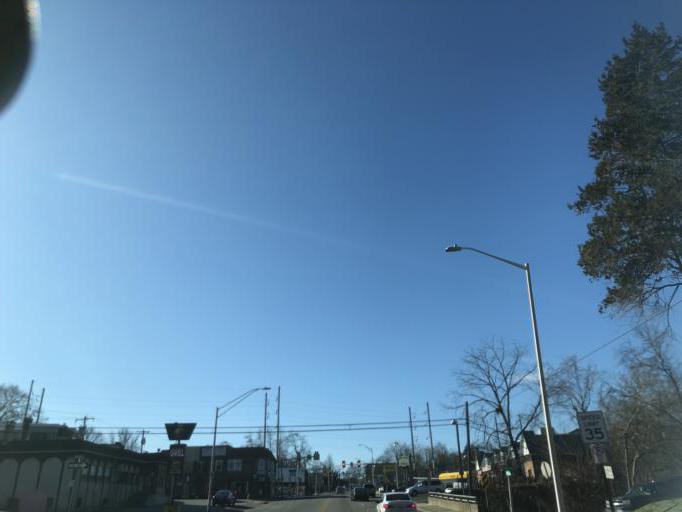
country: US
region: Pennsylvania
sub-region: Delaware County
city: East Lansdowne
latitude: 39.9520
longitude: -75.2651
